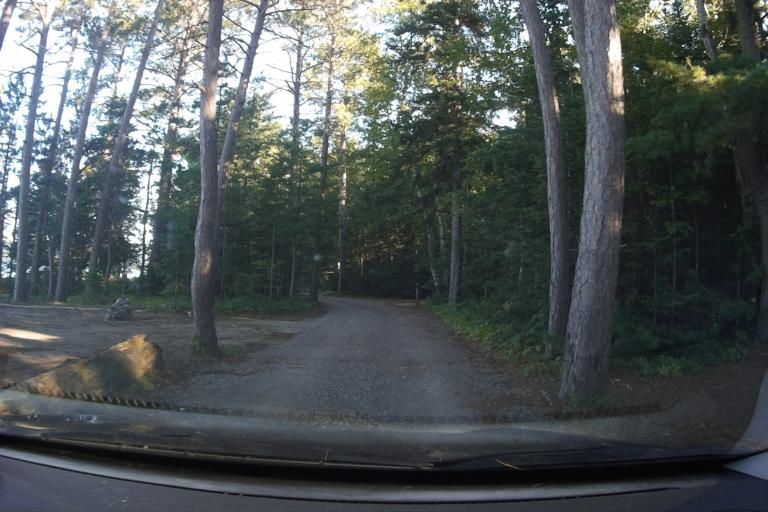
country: CA
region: Ontario
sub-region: Algoma
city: Sault Ste. Marie
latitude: 47.3234
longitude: -84.6103
